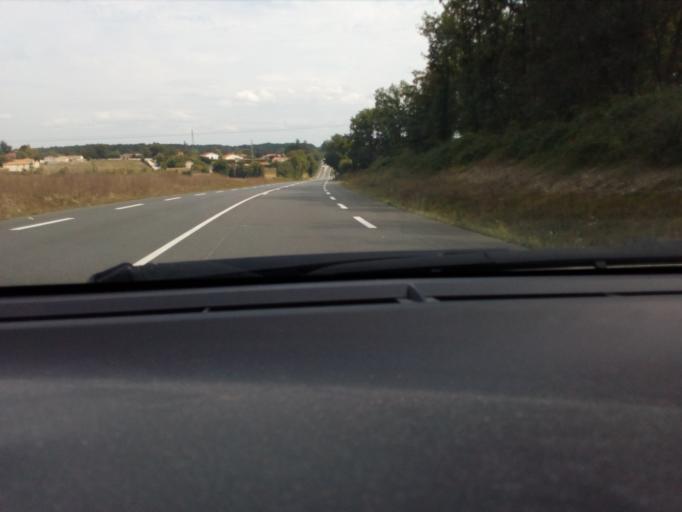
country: FR
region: Poitou-Charentes
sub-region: Departement de la Charente
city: Fleac
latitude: 45.6796
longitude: 0.0781
